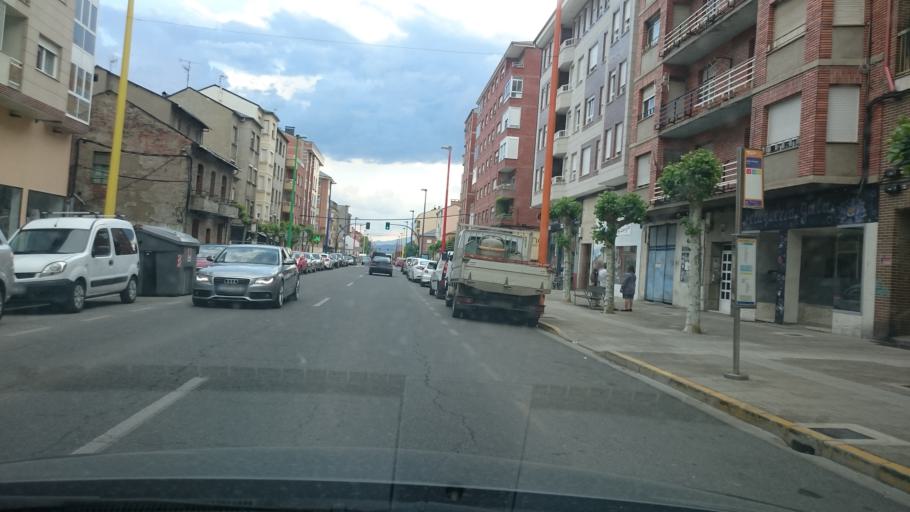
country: ES
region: Castille and Leon
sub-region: Provincia de Leon
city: Ponferrada
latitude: 42.5448
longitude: -6.6173
